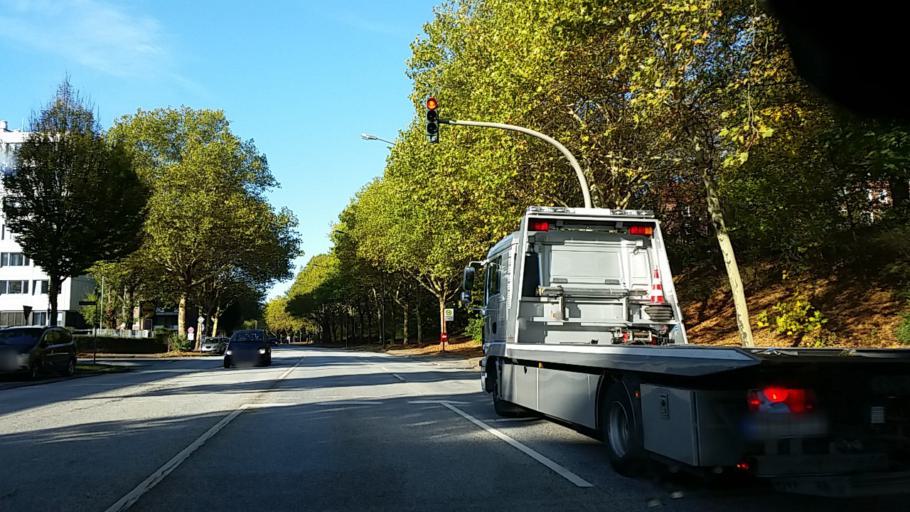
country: DE
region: Hamburg
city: Marienthal
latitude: 53.5545
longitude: 10.0619
